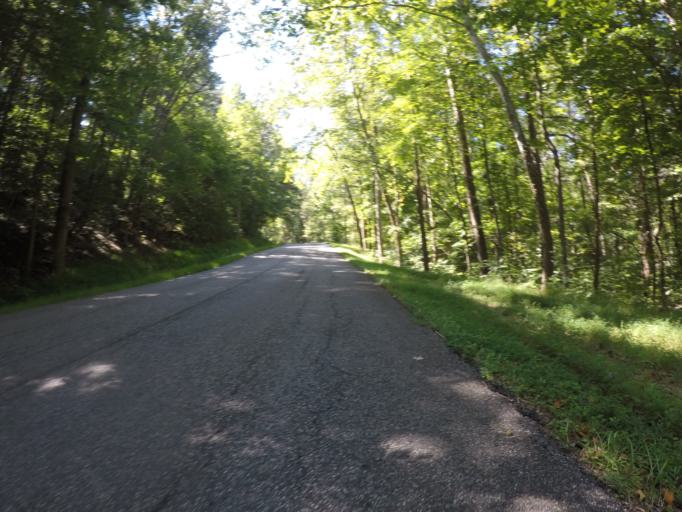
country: US
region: Kentucky
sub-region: Boyd County
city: Ironville
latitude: 38.4205
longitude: -82.6625
